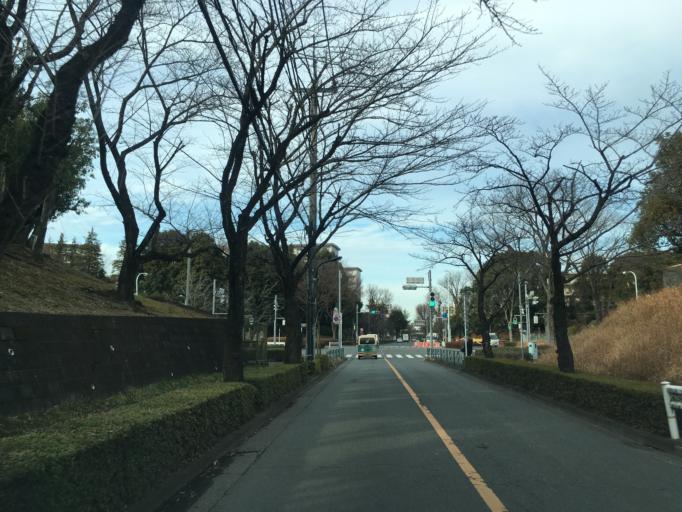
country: JP
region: Tokyo
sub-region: Machida-shi
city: Machida
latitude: 35.6101
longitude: 139.4381
